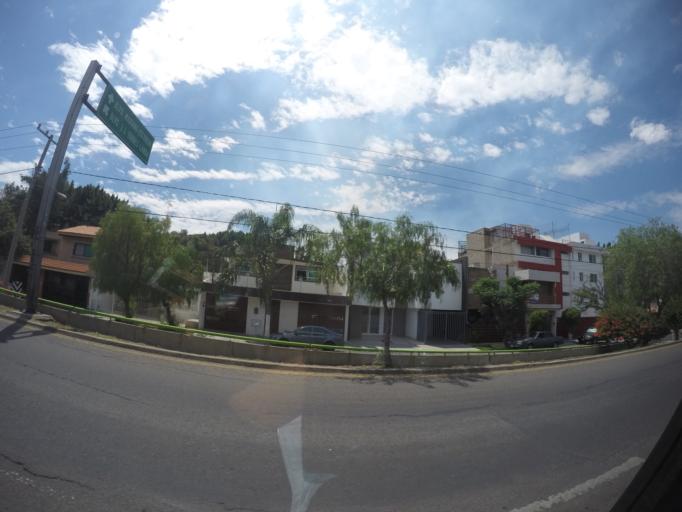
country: MX
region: Guanajuato
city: Leon
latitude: 21.1122
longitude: -101.6646
